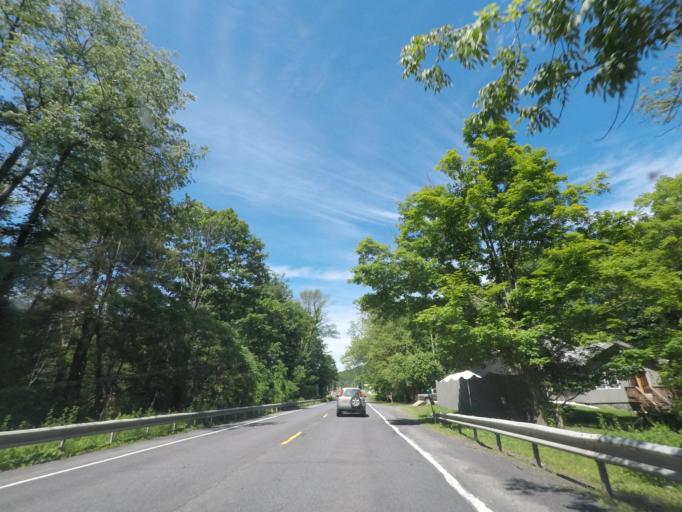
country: US
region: Massachusetts
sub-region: Berkshire County
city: Richmond
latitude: 42.3917
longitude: -73.4143
